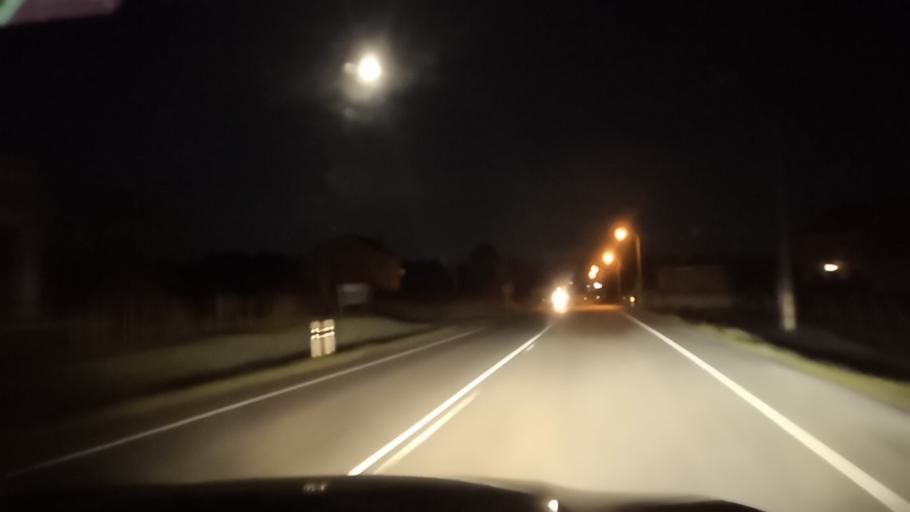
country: ES
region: Galicia
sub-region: Provincia de Ourense
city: Verin
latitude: 41.9448
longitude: -7.4788
